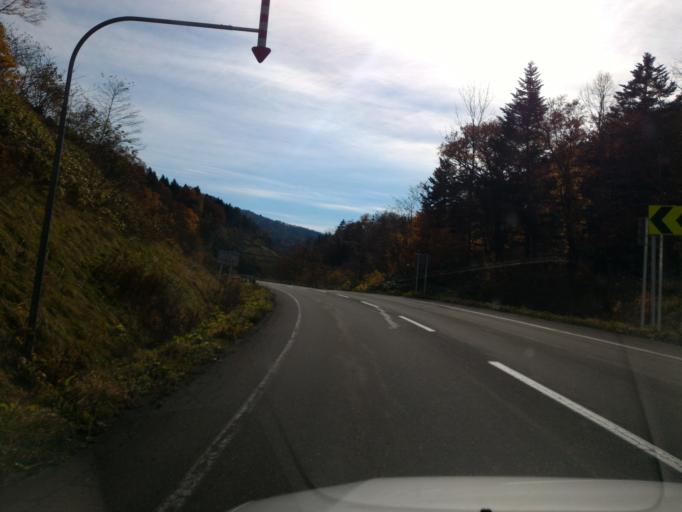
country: JP
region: Hokkaido
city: Shimo-furano
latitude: 43.3591
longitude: 142.2422
